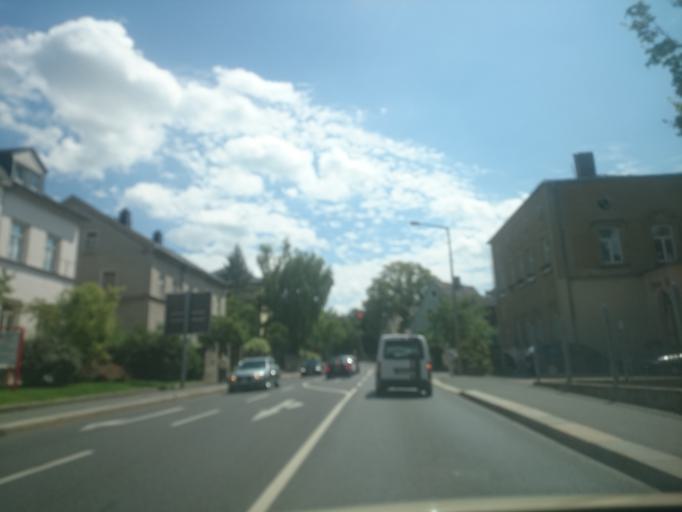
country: DE
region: Saxony
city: Freiberg
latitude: 50.9133
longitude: 13.3384
